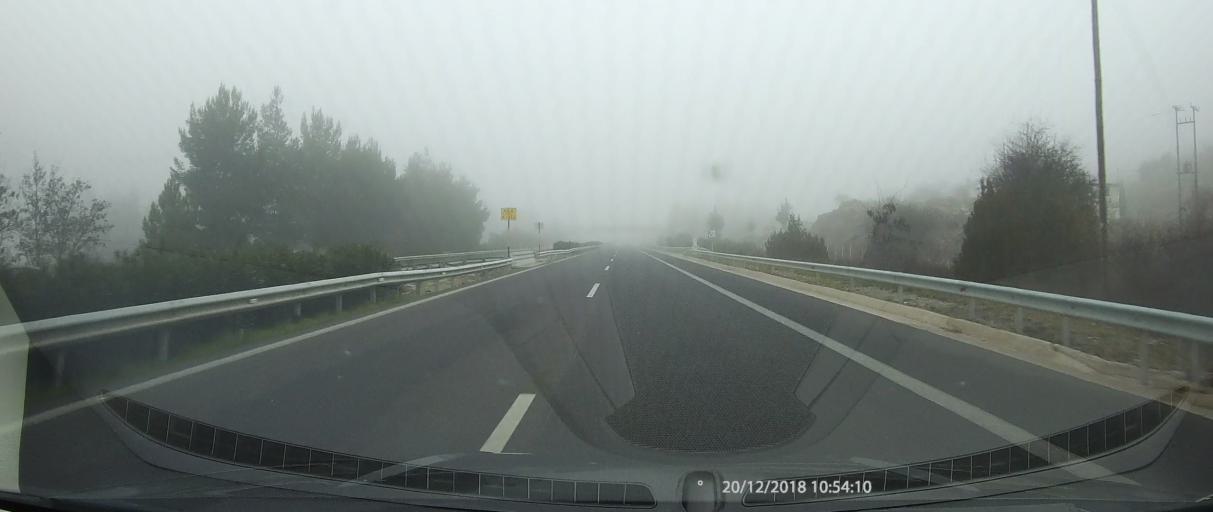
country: GR
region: Peloponnese
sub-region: Nomos Arkadias
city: Tripoli
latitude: 37.6231
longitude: 22.4635
